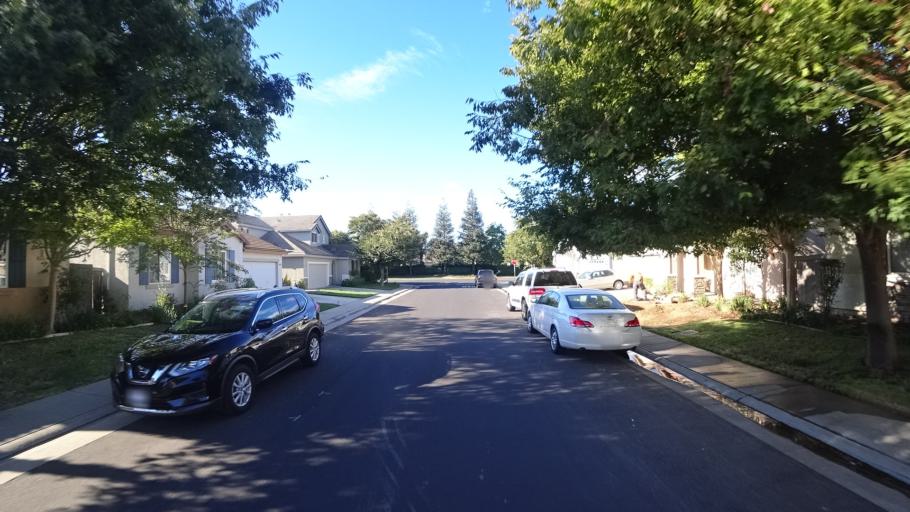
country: US
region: California
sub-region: Sacramento County
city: Laguna
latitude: 38.4053
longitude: -121.4753
